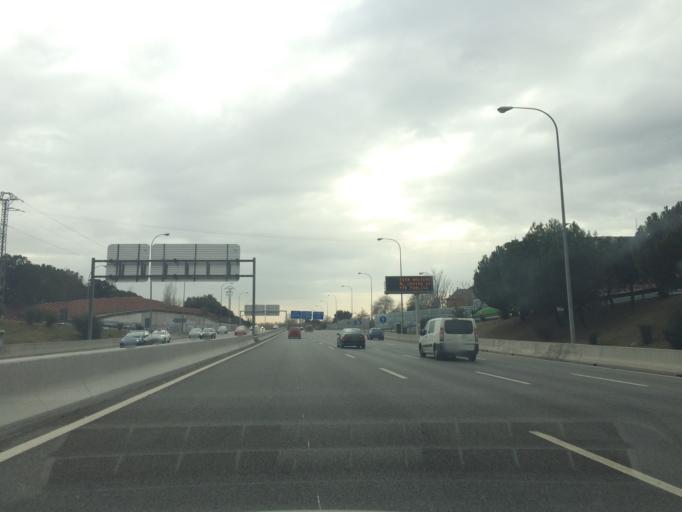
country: ES
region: Madrid
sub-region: Provincia de Madrid
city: Tetuan de las Victorias
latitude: 40.4689
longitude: -3.7500
